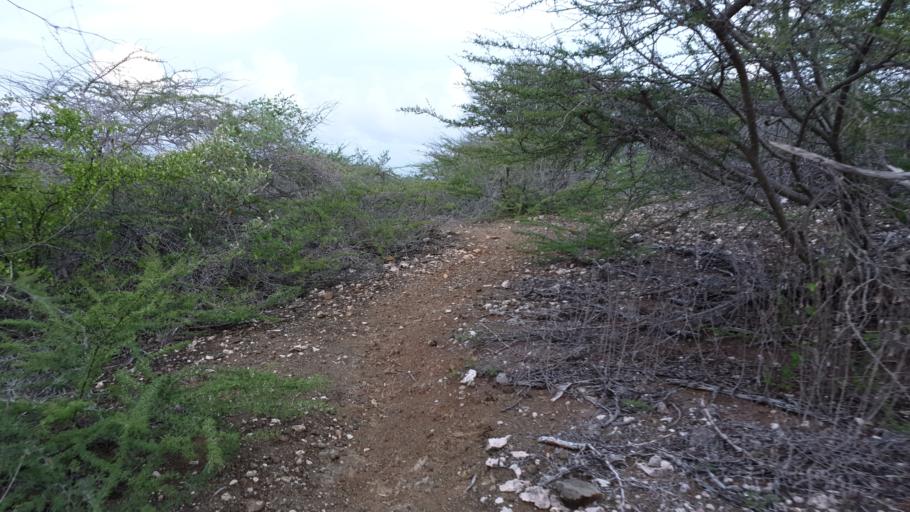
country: CW
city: Newport
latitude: 12.1270
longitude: -68.8144
